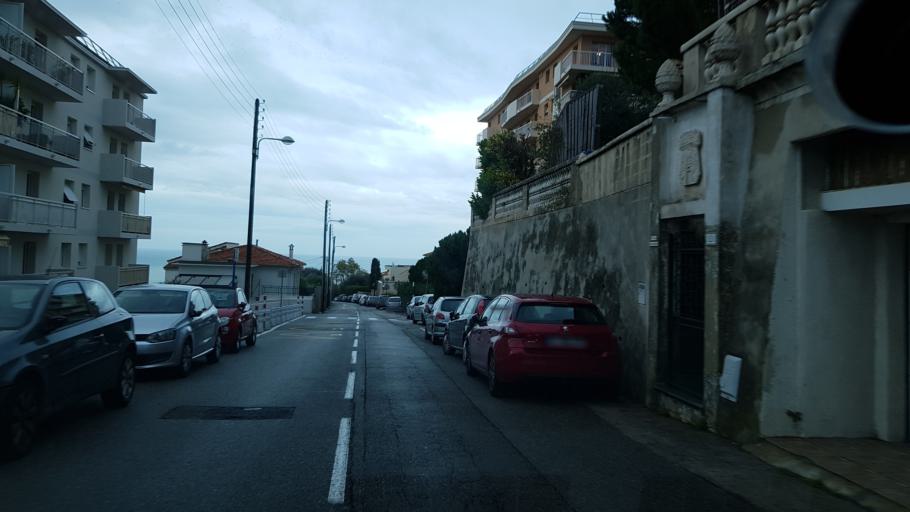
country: FR
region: Provence-Alpes-Cote d'Azur
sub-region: Departement des Alpes-Maritimes
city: Nice
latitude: 43.6992
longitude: 7.2350
